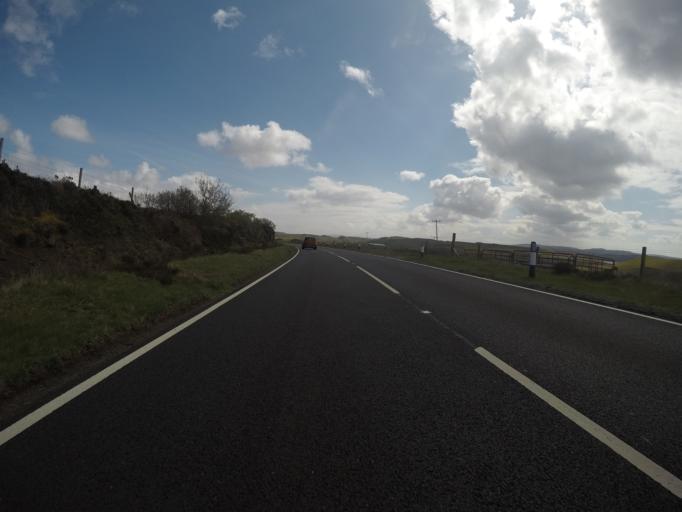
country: GB
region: Scotland
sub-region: Highland
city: Portree
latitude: 57.5354
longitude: -6.3607
